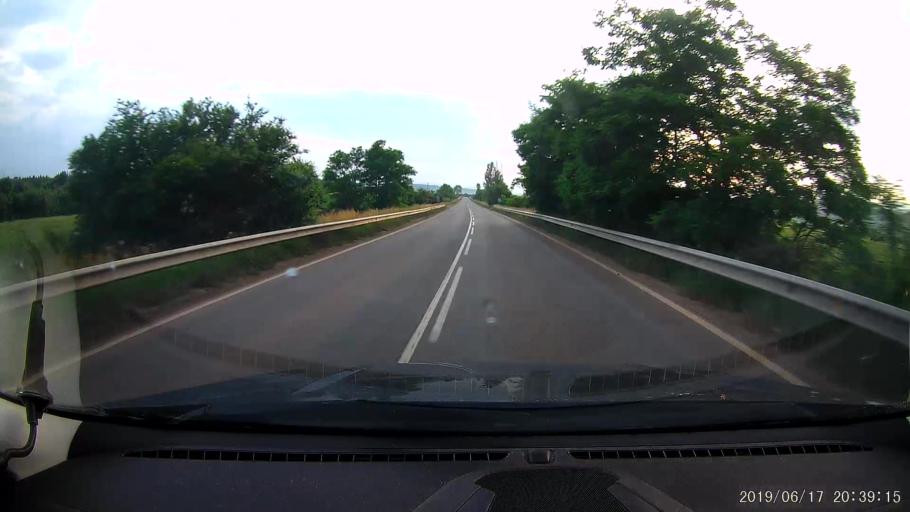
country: BG
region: Sofiya
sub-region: Obshtina Slivnitsa
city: Slivnitsa
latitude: 42.8817
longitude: 23.0116
